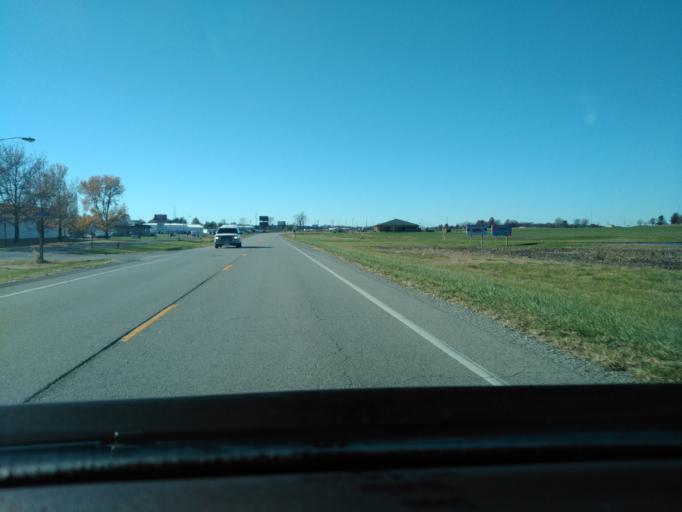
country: US
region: Illinois
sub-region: Madison County
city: Highland
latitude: 38.7443
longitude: -89.6905
